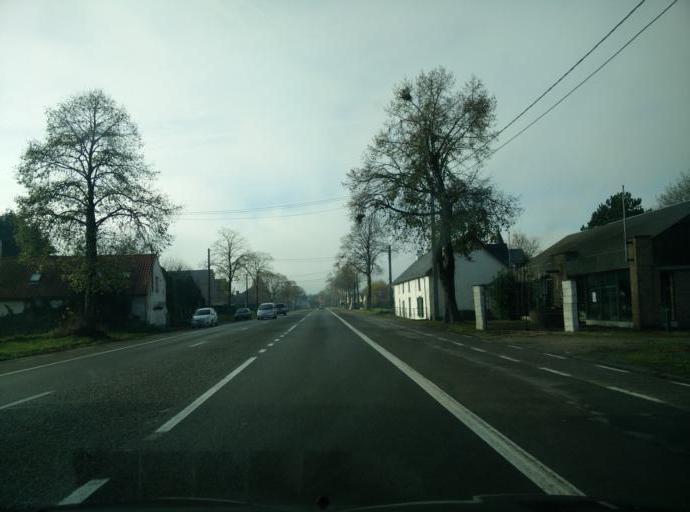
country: BE
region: Wallonia
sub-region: Province du Brabant Wallon
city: Rebecq-Rognon
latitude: 50.6919
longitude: 4.0925
